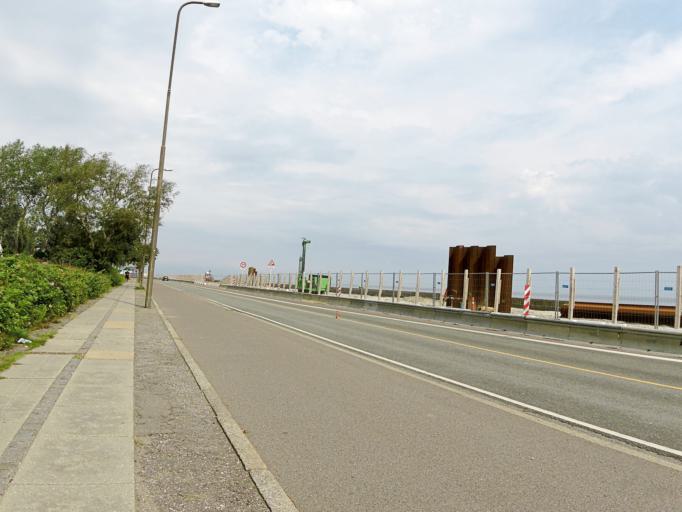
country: DK
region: Capital Region
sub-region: Gentofte Kommune
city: Charlottenlund
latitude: 55.7692
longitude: 12.5961
